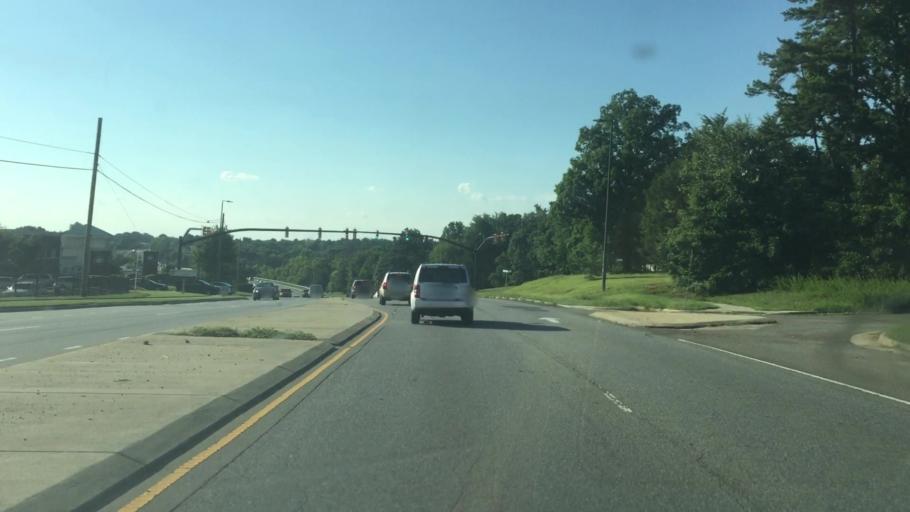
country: US
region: North Carolina
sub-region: Cabarrus County
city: Kannapolis
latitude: 35.4147
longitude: -80.6675
